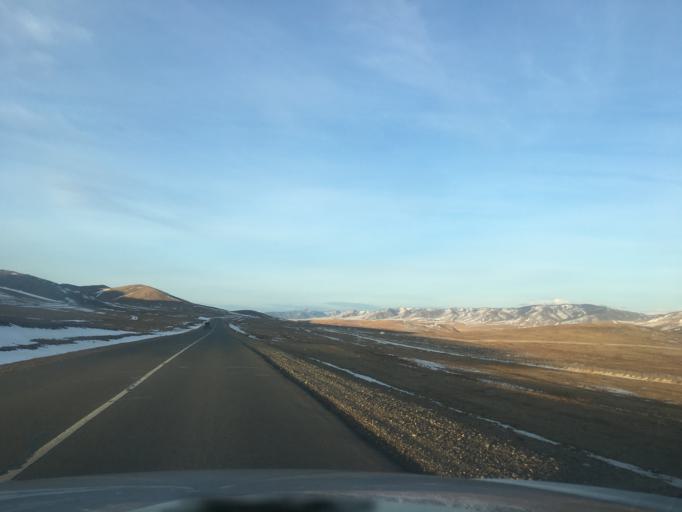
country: MN
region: Central Aimak
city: Mandal
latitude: 48.2181
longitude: 106.7116
